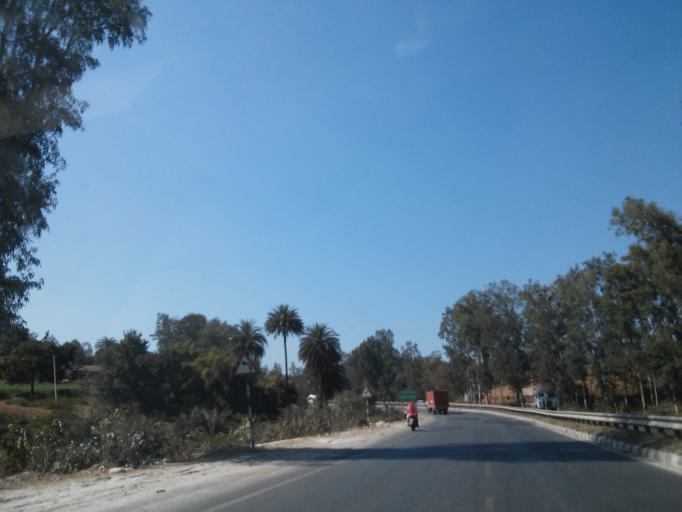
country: IN
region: Rajasthan
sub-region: Dungarpur
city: Dungarpur
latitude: 23.7746
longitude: 73.5072
